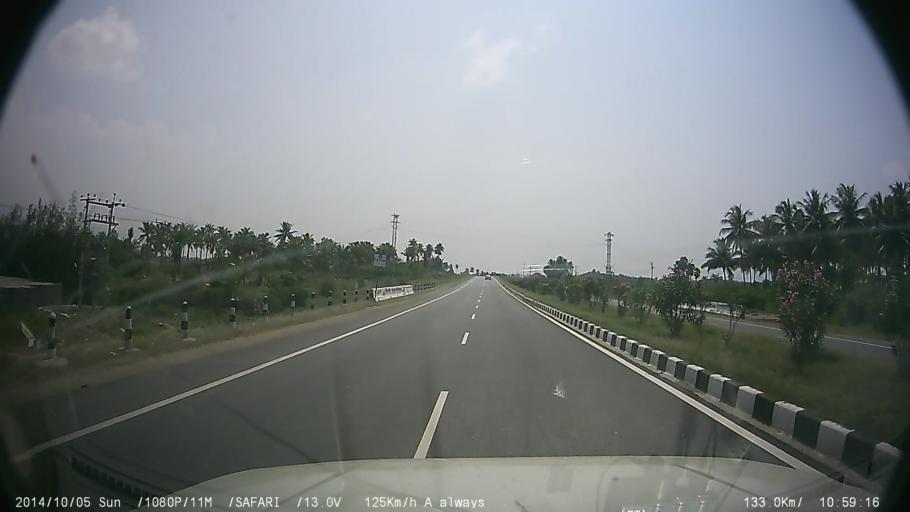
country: IN
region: Tamil Nadu
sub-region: Salem
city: Attur
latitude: 11.6364
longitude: 78.5280
